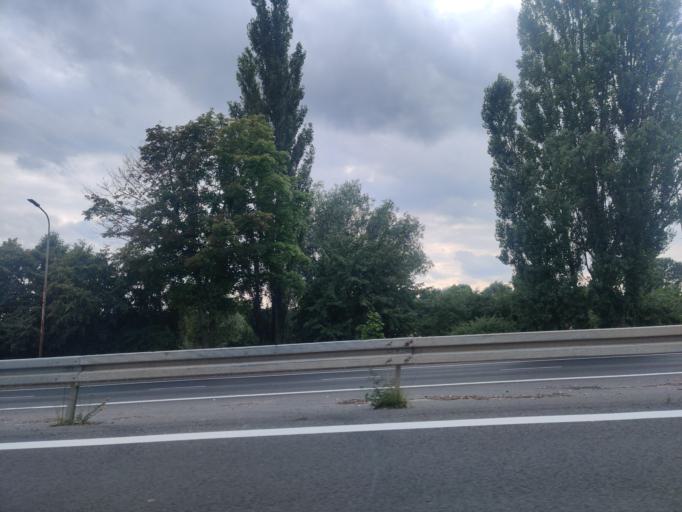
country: PL
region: Greater Poland Voivodeship
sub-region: Konin
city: Konin
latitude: 52.2086
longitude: 18.2647
